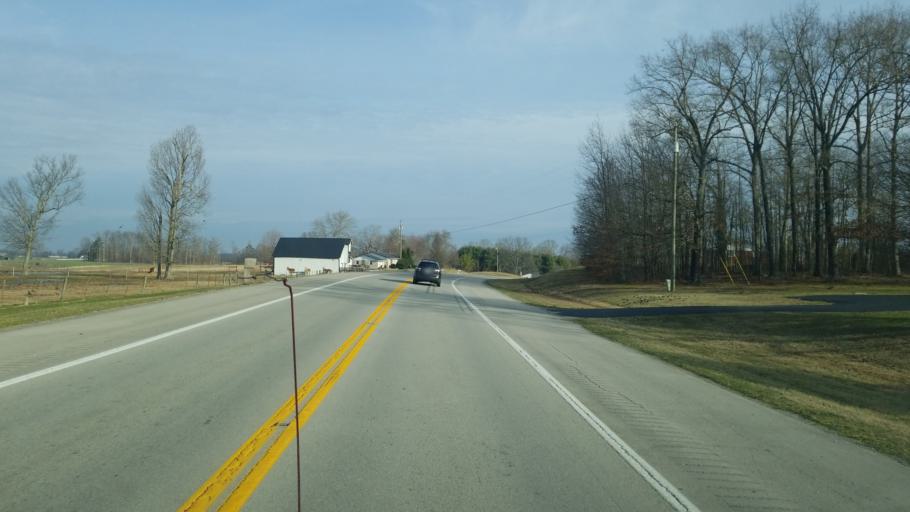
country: US
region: Kentucky
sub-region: Russell County
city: Russell Springs
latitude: 37.1424
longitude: -85.0314
